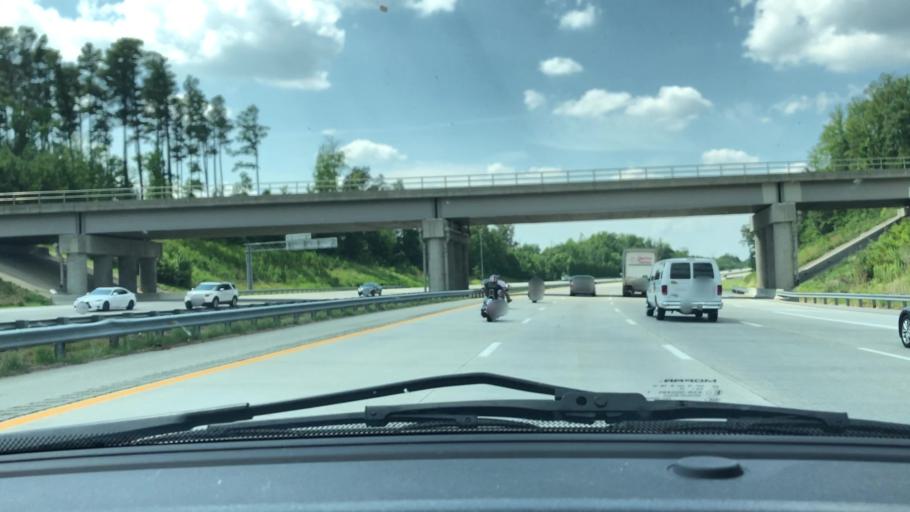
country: US
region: North Carolina
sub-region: Guilford County
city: Jamestown
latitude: 36.0288
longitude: -79.8855
